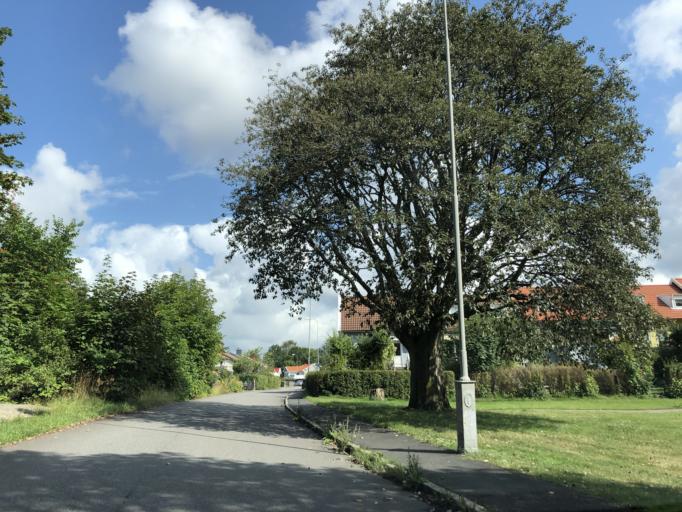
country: SE
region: Vaestra Goetaland
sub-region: Goteborg
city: Majorna
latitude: 57.7175
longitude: 11.9004
